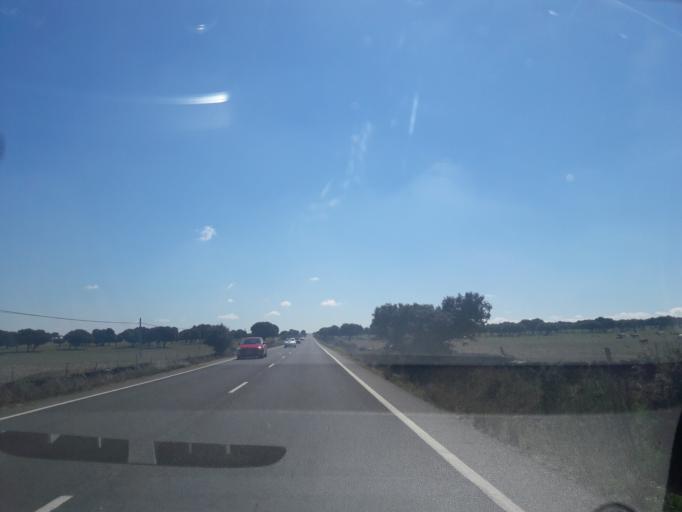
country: ES
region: Castille and Leon
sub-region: Provincia de Salamanca
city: Doninos de Ledesma
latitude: 41.0261
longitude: -6.0055
